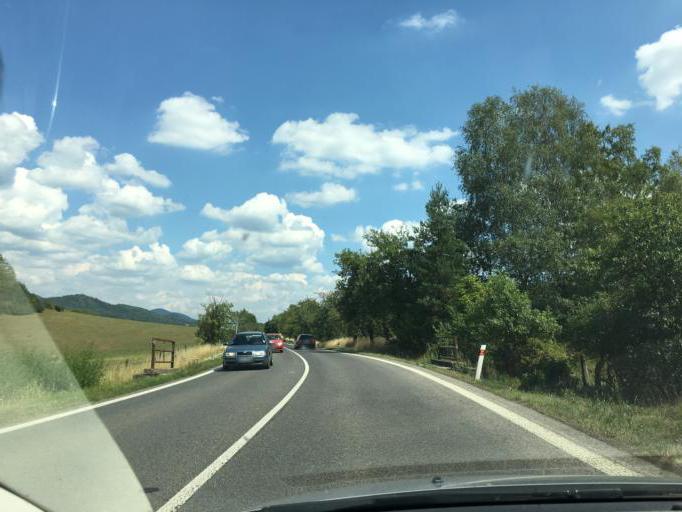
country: CZ
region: Ustecky
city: Ceska Kamenice
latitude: 50.7921
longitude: 14.3912
